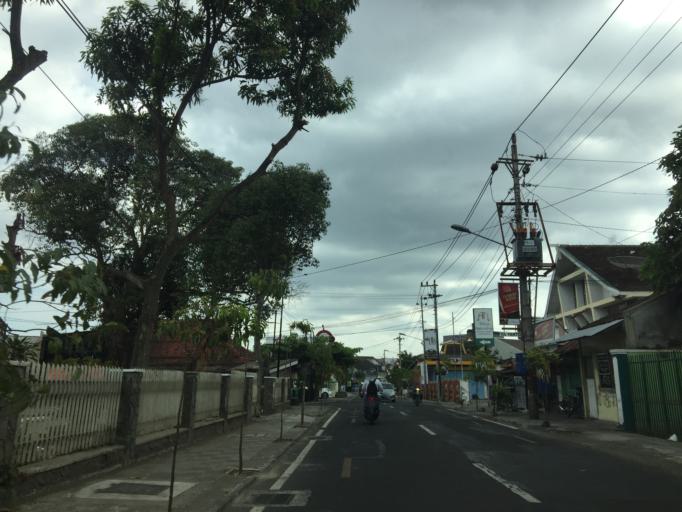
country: ID
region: Daerah Istimewa Yogyakarta
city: Yogyakarta
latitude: -7.7786
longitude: 110.3636
